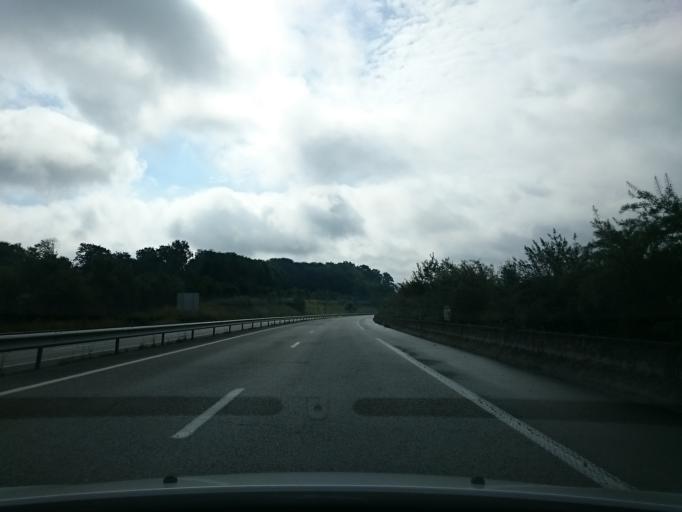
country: FR
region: Lower Normandy
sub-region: Departement du Calvados
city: Saint-Desir
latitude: 49.1362
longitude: 0.1747
